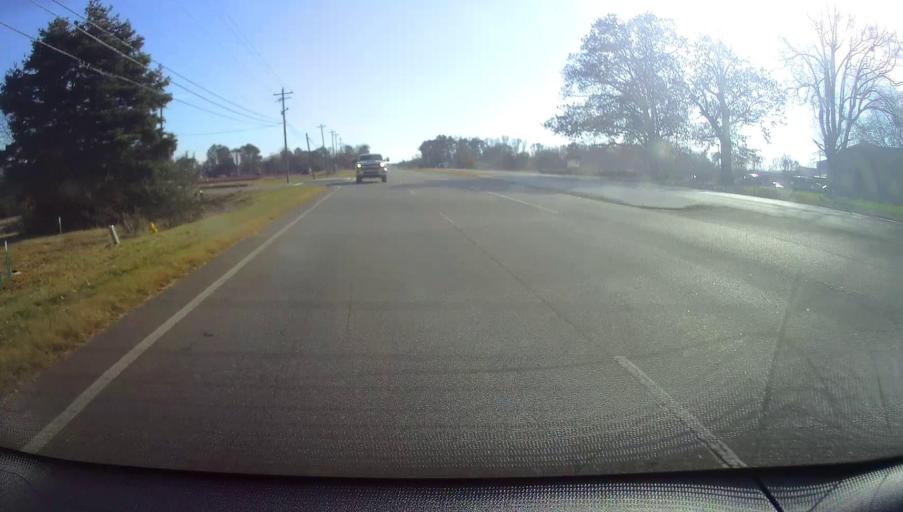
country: US
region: Alabama
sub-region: Limestone County
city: Athens
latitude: 34.7601
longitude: -86.9570
